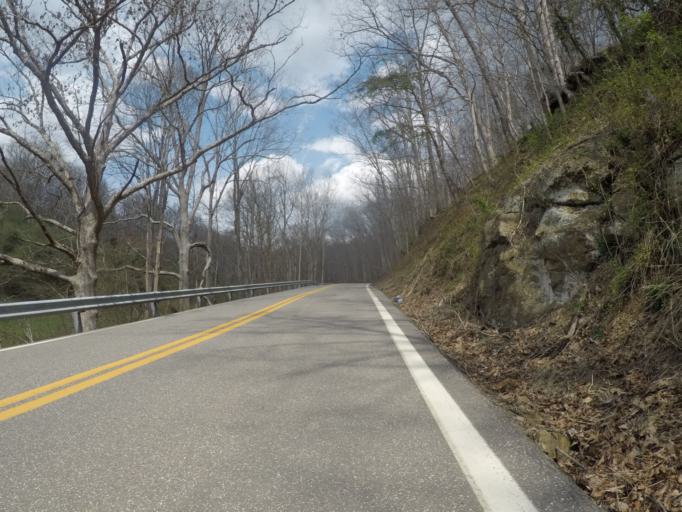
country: US
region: West Virginia
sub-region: Cabell County
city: Pea Ridge
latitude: 38.3480
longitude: -82.3360
